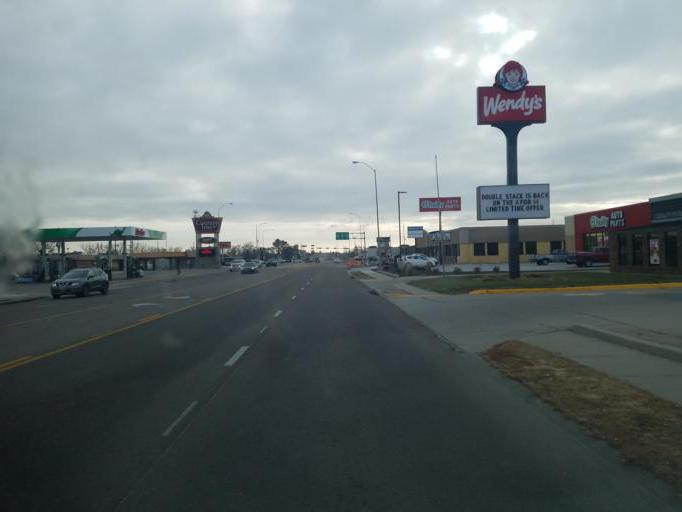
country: US
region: Nebraska
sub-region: Madison County
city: Norfolk
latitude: 42.0201
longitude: -97.4266
